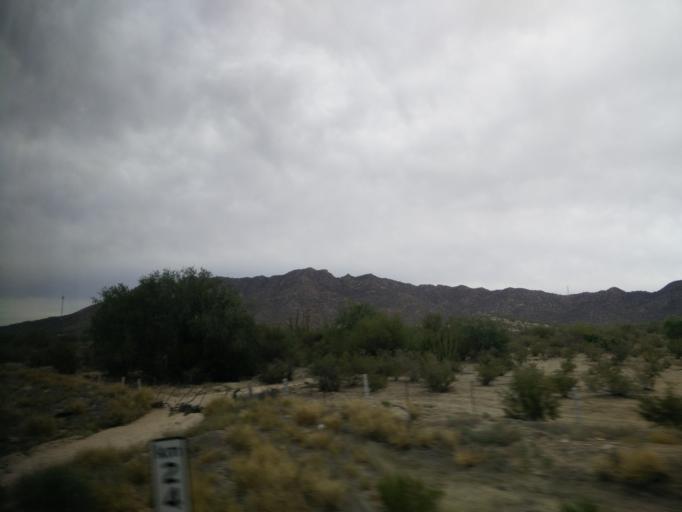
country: MX
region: Sonora
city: Hermosillo
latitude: 28.9601
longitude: -110.9632
